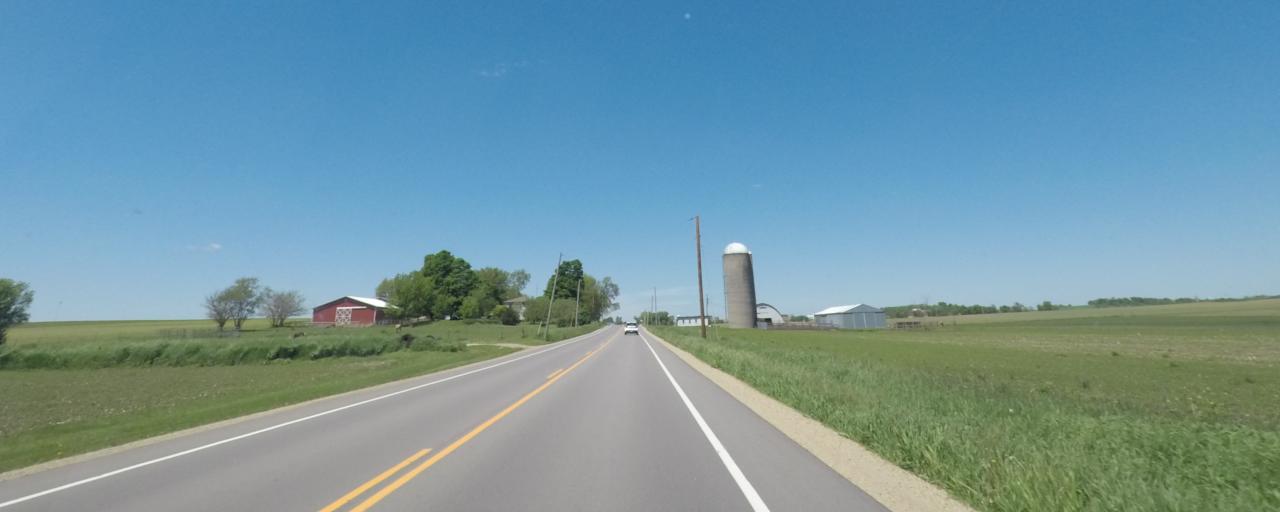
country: US
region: Wisconsin
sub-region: Green County
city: Brooklyn
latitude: 42.8060
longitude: -89.3692
